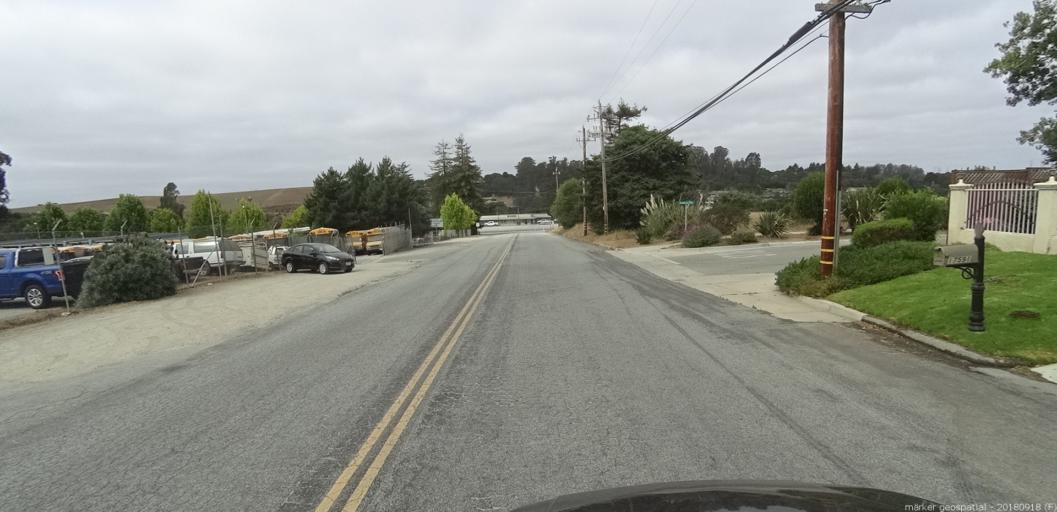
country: US
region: California
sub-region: Monterey County
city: Prunedale
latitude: 36.7763
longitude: -121.6674
